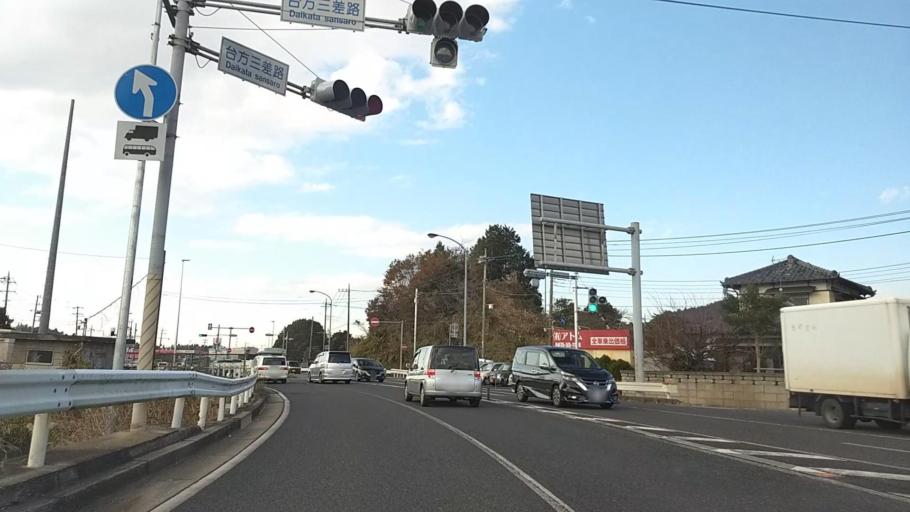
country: JP
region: Chiba
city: Togane
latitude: 35.5592
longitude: 140.3427
